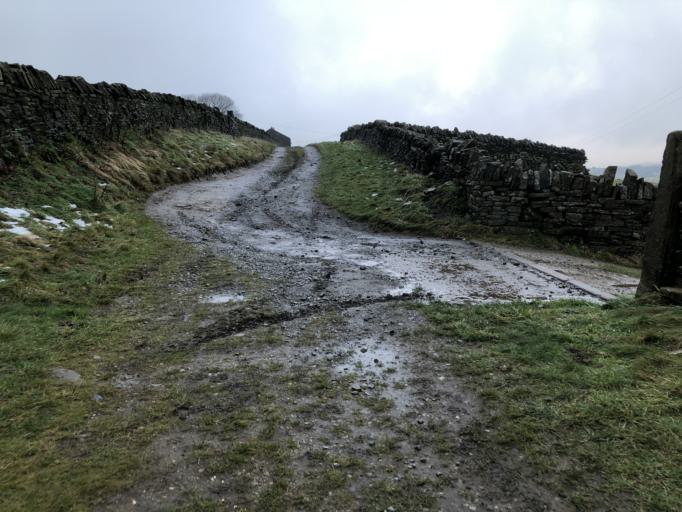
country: GB
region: England
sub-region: Kirklees
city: Holmfirth
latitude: 53.5482
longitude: -1.7951
